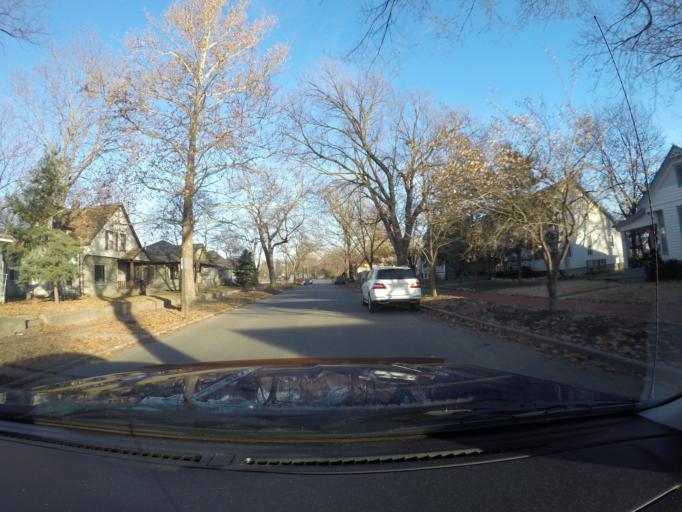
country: US
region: Kansas
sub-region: Riley County
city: Manhattan
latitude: 39.1774
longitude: -96.5727
